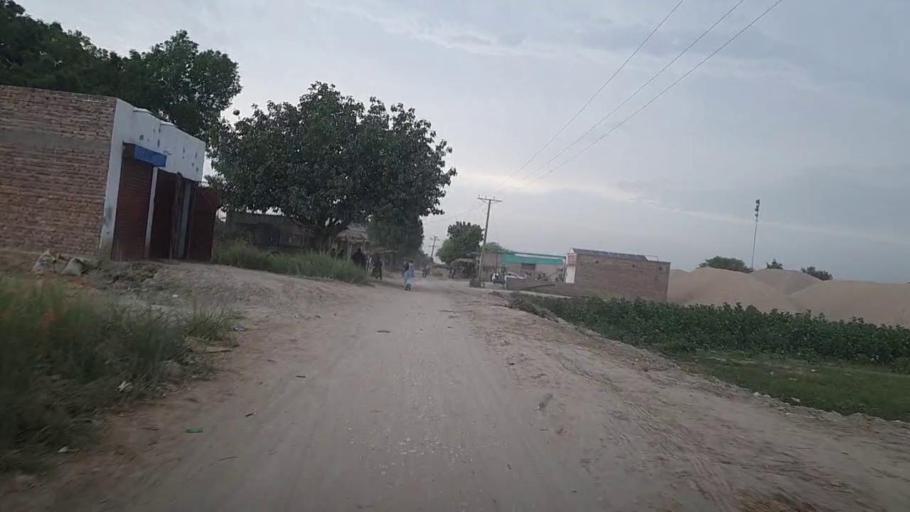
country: PK
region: Sindh
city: Karaundi
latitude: 26.9857
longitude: 68.3437
